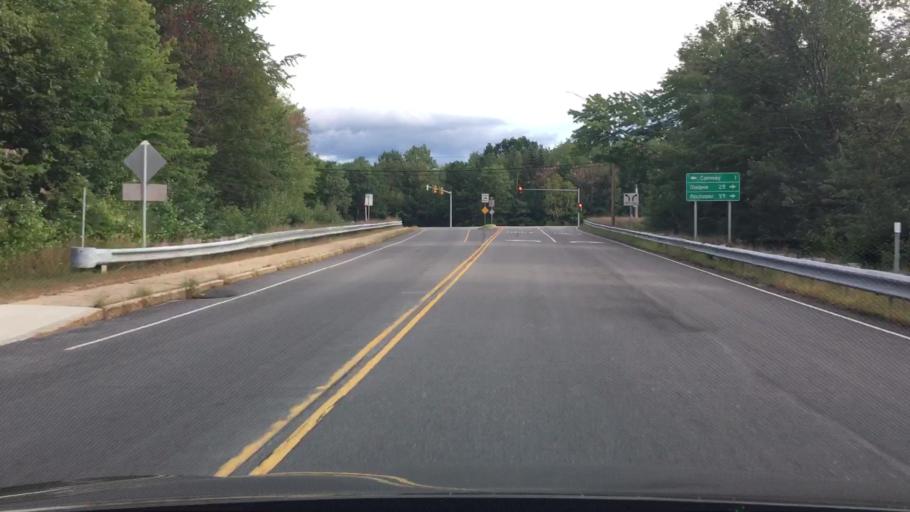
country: US
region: New Hampshire
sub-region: Carroll County
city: Conway
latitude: 43.9791
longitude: -71.1344
